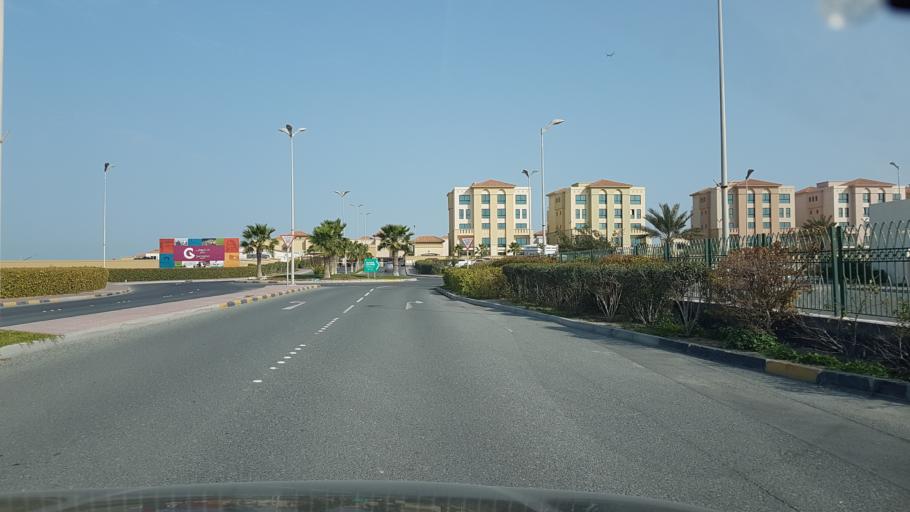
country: BH
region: Muharraq
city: Al Hadd
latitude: 26.2781
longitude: 50.6673
